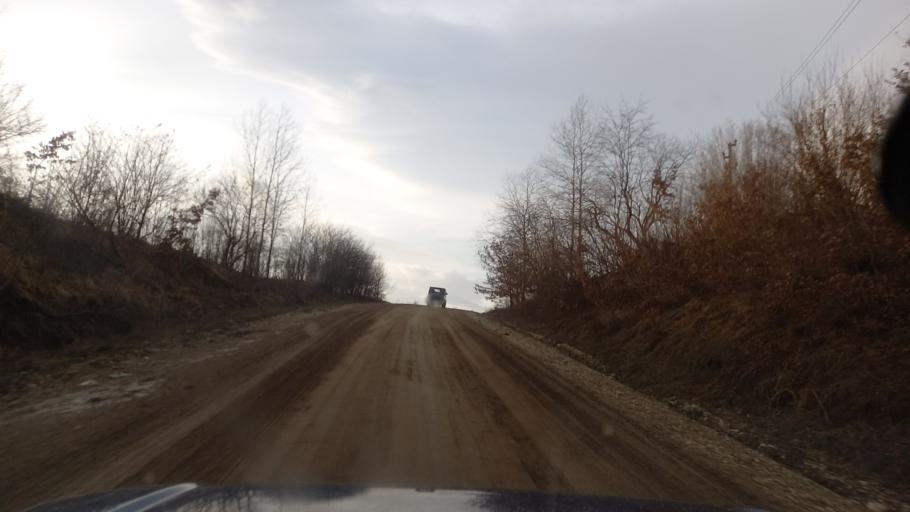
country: RU
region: Adygeya
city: Kamennomostskiy
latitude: 44.1937
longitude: 40.2572
